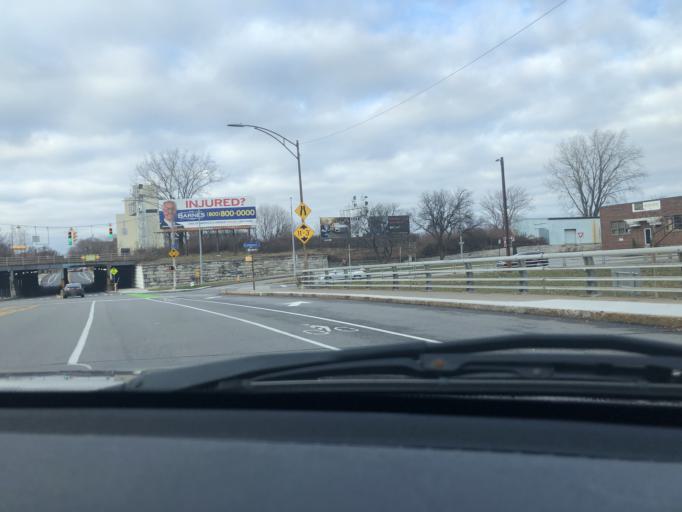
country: US
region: New York
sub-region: Monroe County
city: Rochester
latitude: 43.1613
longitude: -77.6104
